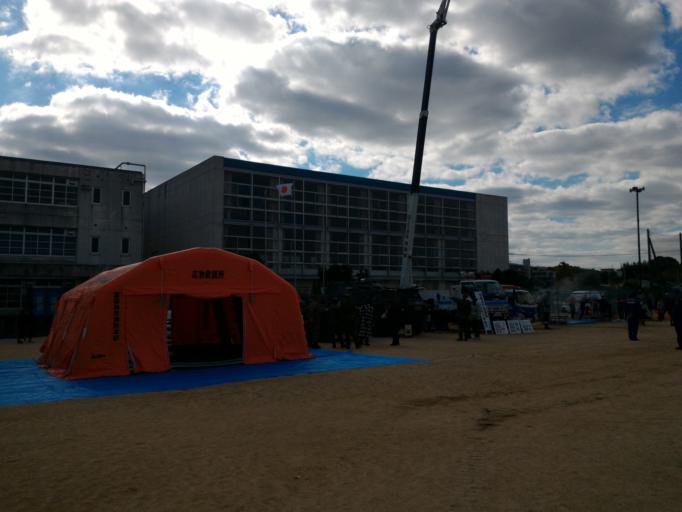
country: JP
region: Osaka
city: Tondabayashicho
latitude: 34.4967
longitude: 135.5802
